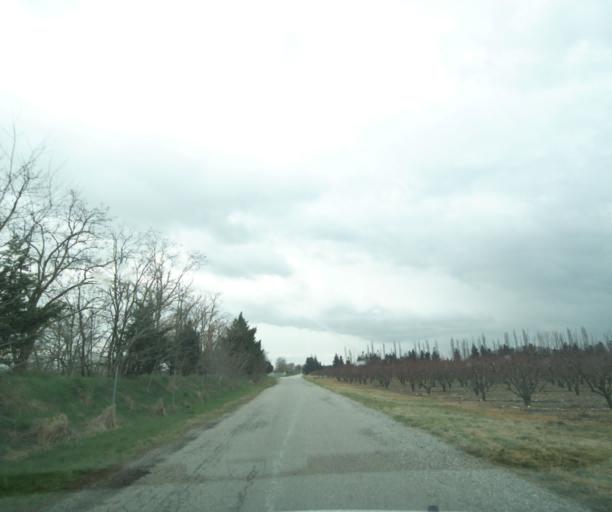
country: FR
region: Rhone-Alpes
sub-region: Departement de la Drome
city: Bourg-les-Valence
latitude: 44.9798
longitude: 4.8887
